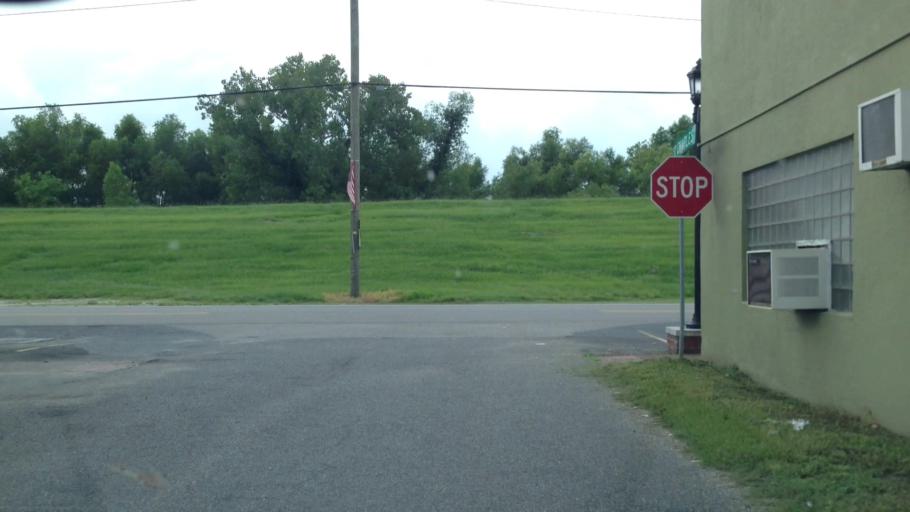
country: US
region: Louisiana
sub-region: Saint Charles Parish
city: Norco
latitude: 29.9969
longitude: -90.4130
